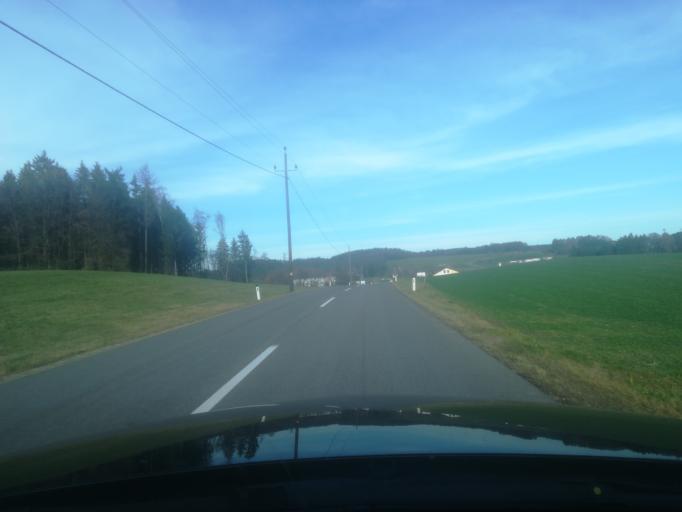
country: AT
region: Upper Austria
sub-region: Politischer Bezirk Perg
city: Perg
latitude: 48.3162
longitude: 14.6623
